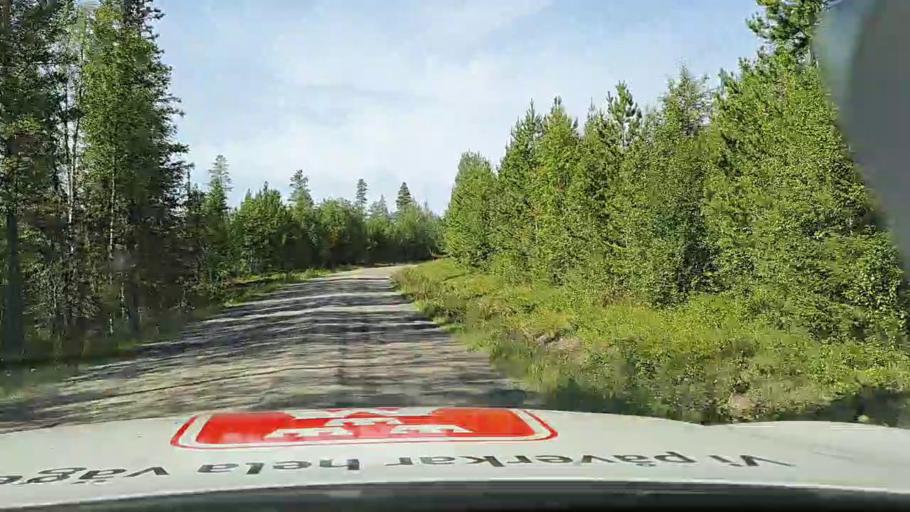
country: SE
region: Jaemtland
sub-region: Stroemsunds Kommun
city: Stroemsund
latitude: 63.7202
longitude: 15.2746
